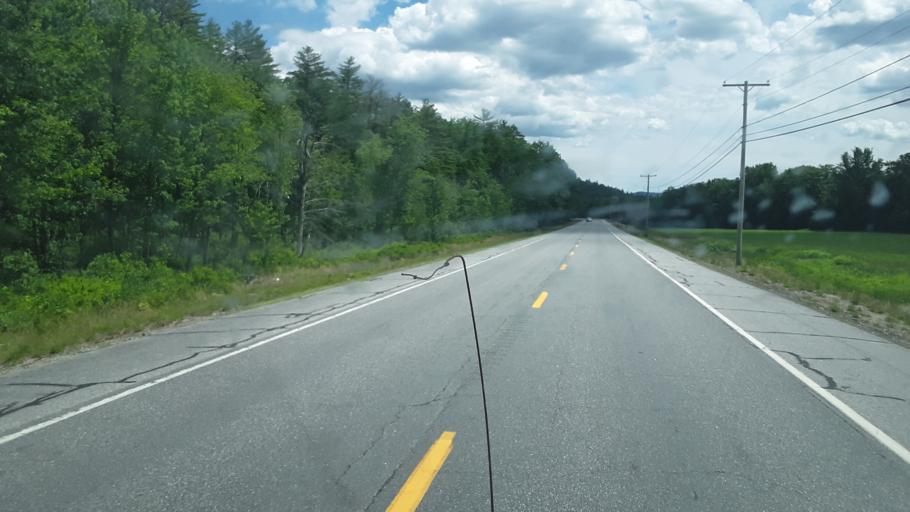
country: US
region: Maine
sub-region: Oxford County
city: Rumford
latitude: 44.4915
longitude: -70.6532
